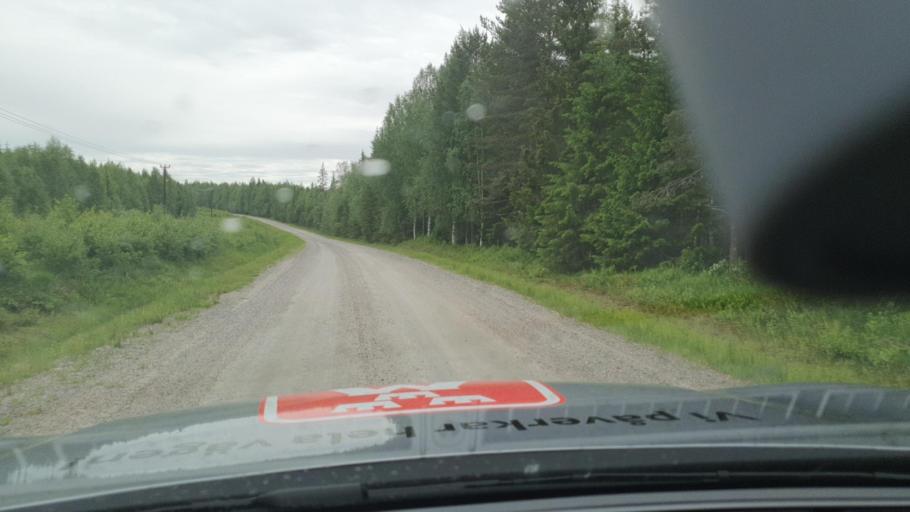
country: SE
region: Norrbotten
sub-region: Kalix Kommun
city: Rolfs
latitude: 66.0518
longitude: 23.0283
